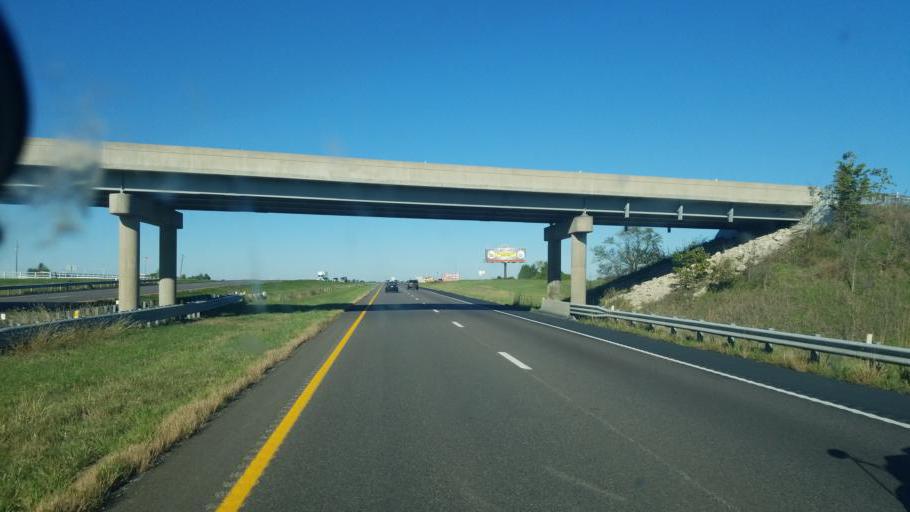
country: US
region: Missouri
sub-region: Callaway County
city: Fulton
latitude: 38.9396
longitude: -91.8651
